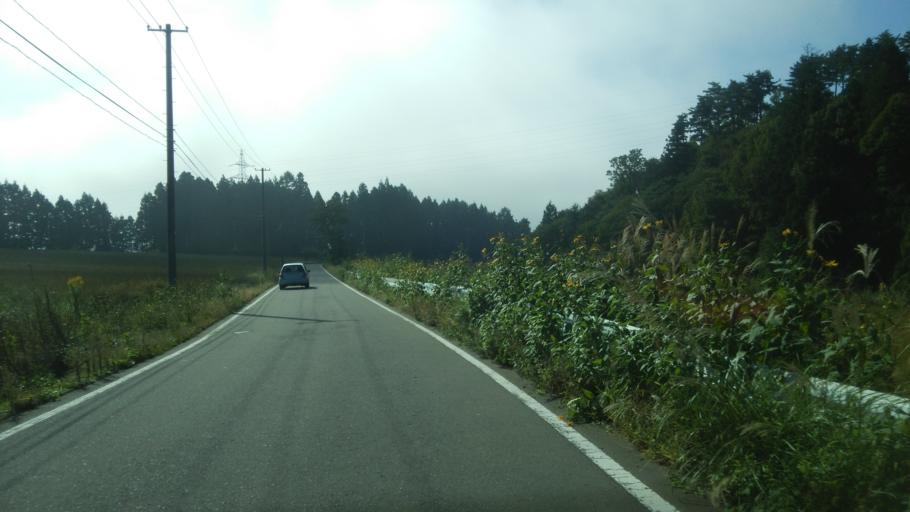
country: JP
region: Fukushima
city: Kitakata
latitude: 37.5851
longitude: 139.9460
